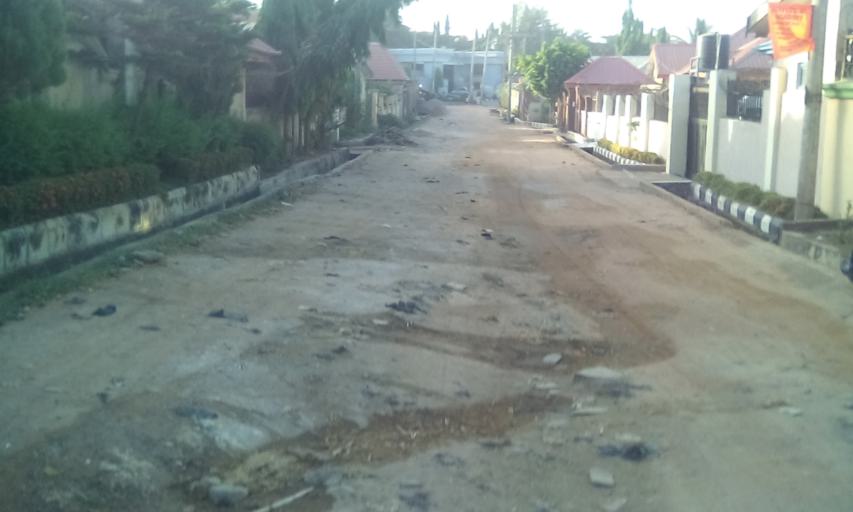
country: NG
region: Abuja Federal Capital Territory
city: Abuja
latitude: 8.9890
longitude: 7.3546
